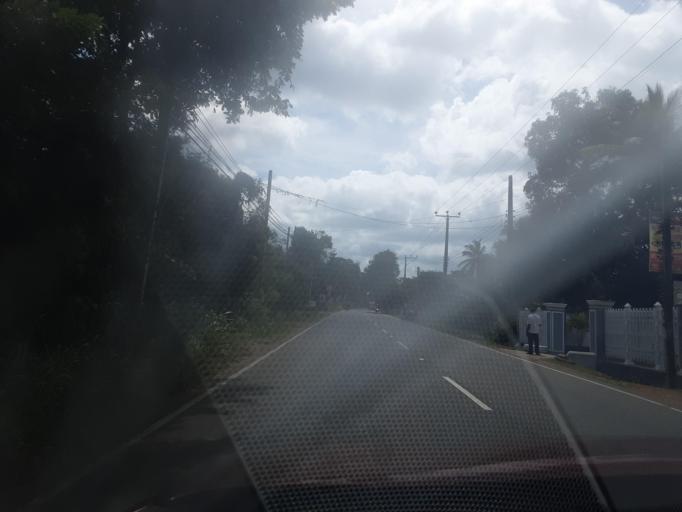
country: LK
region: North Western
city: Kuliyapitiya
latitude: 7.4810
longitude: 79.9942
